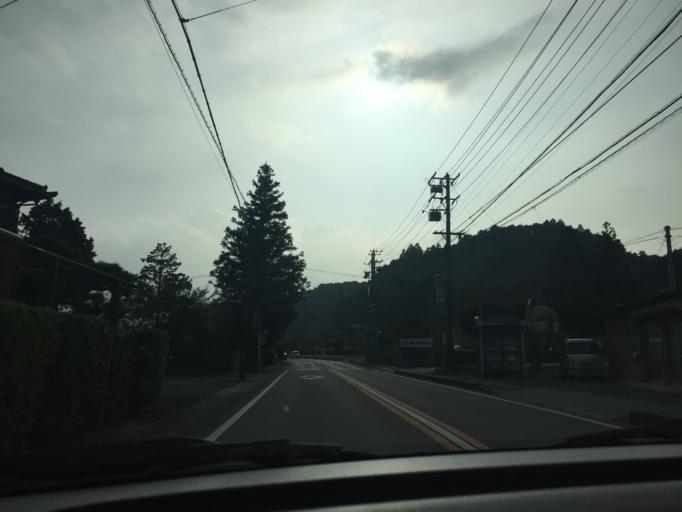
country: JP
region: Aichi
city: Shinshiro
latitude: 34.9294
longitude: 137.5669
